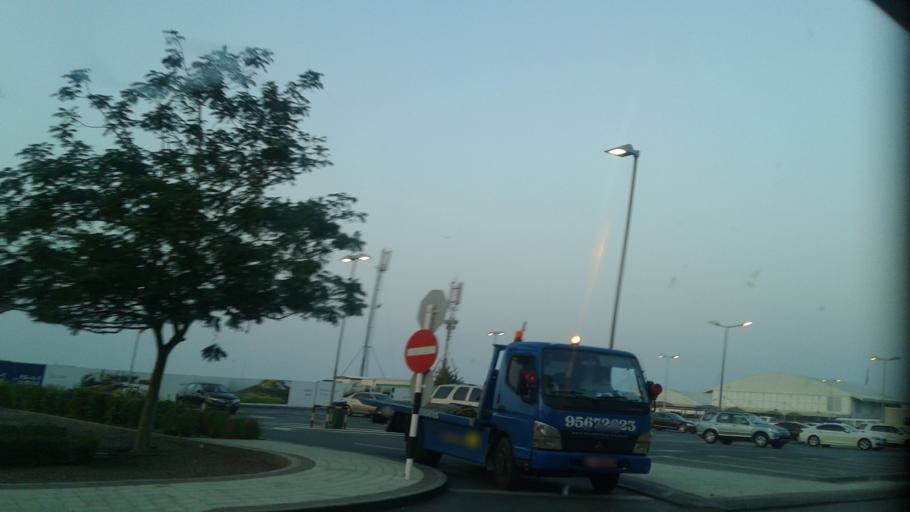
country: OM
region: Muhafazat Masqat
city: As Sib al Jadidah
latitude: 23.6299
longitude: 58.2649
